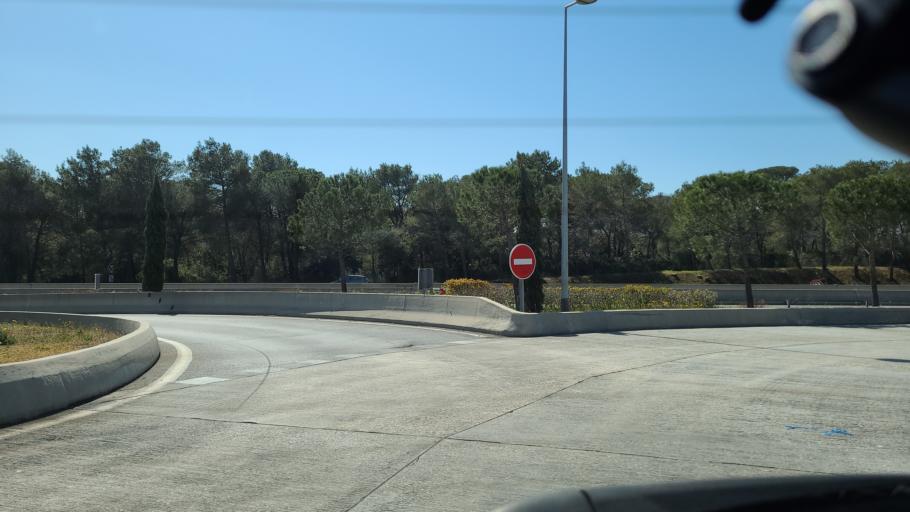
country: FR
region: Provence-Alpes-Cote d'Azur
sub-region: Departement du Var
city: Puget-sur-Argens
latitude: 43.4666
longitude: 6.6726
